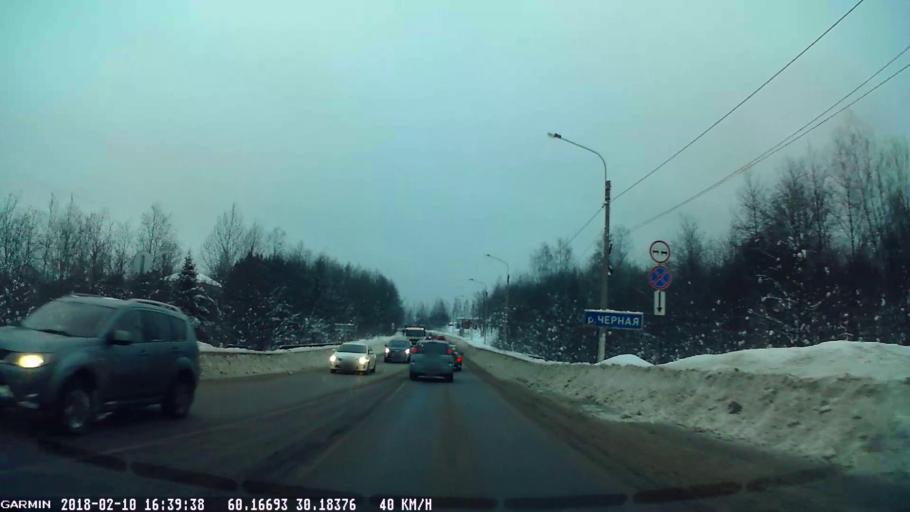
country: RU
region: Leningrad
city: Sertolovo
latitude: 60.1578
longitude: 30.1880
